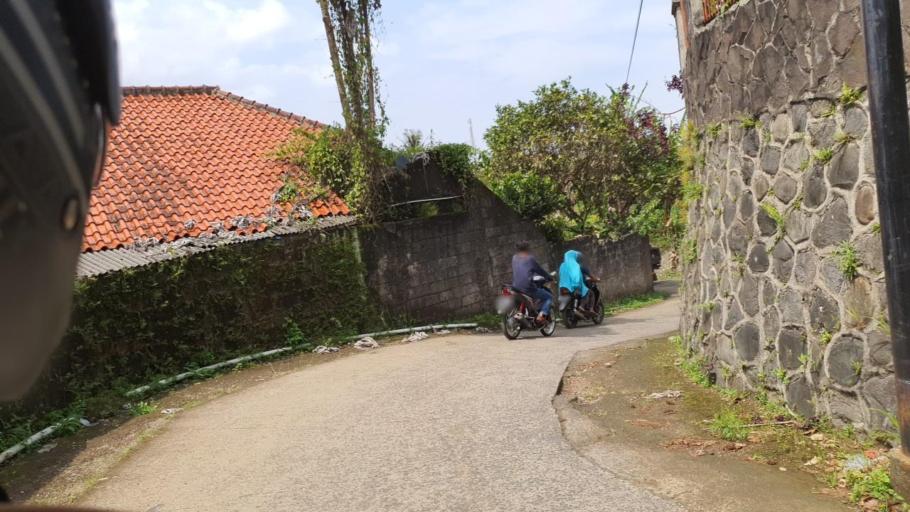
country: ID
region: West Java
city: Caringin
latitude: -6.6459
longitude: 106.8889
